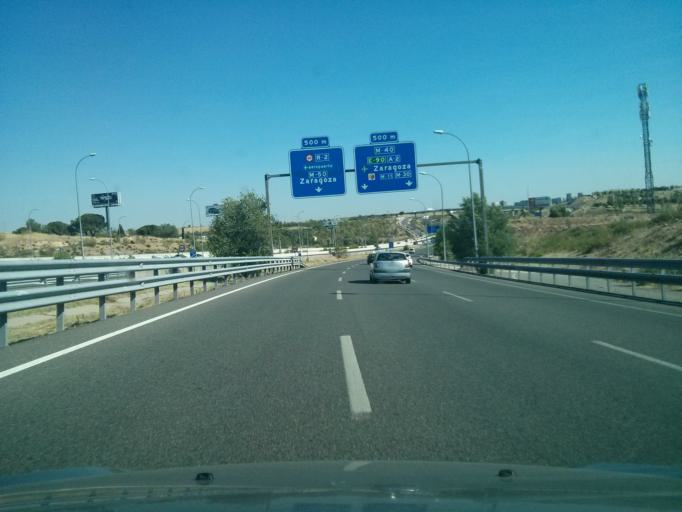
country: ES
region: Madrid
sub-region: Provincia de Madrid
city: Las Tablas
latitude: 40.5057
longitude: -3.6499
